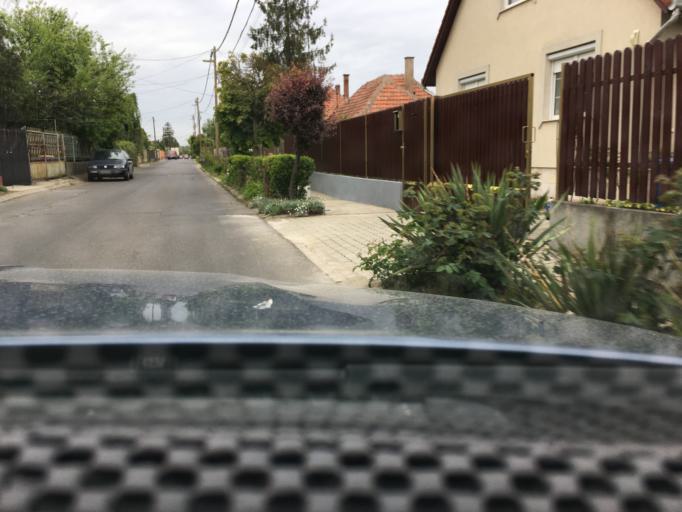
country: HU
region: Hajdu-Bihar
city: Debrecen
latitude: 47.5391
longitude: 21.6646
